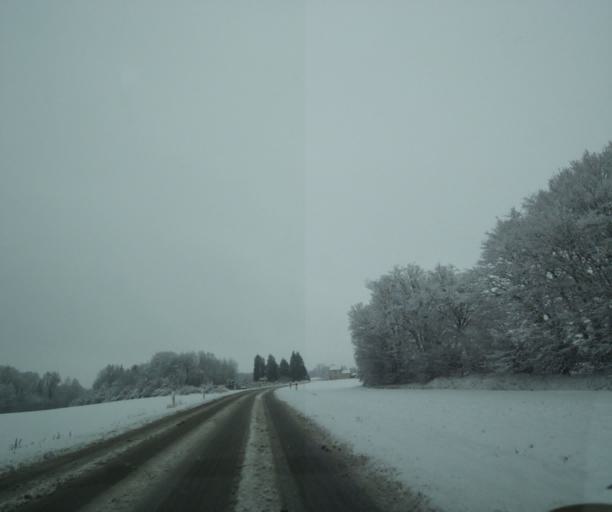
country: FR
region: Champagne-Ardenne
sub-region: Departement de la Haute-Marne
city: Saint-Dizier
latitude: 48.5906
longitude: 4.9022
